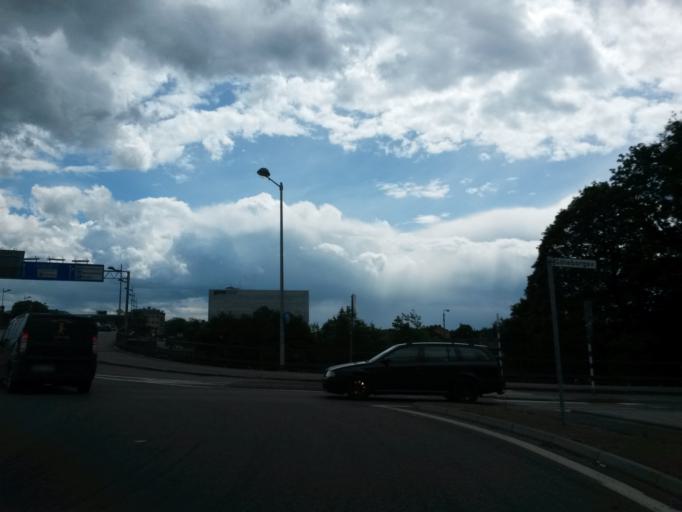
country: SE
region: Vaestra Goetaland
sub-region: Boras Kommun
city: Boras
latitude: 57.7212
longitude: 12.9293
